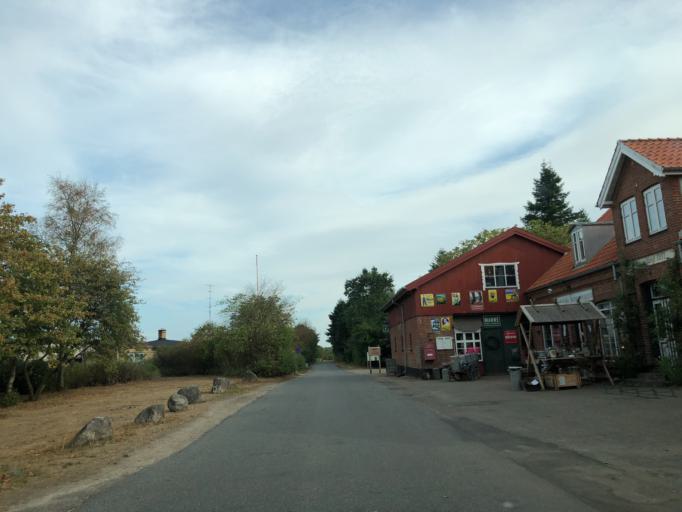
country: DK
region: South Denmark
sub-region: Vejle Kommune
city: Egtved
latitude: 55.6570
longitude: 9.2601
